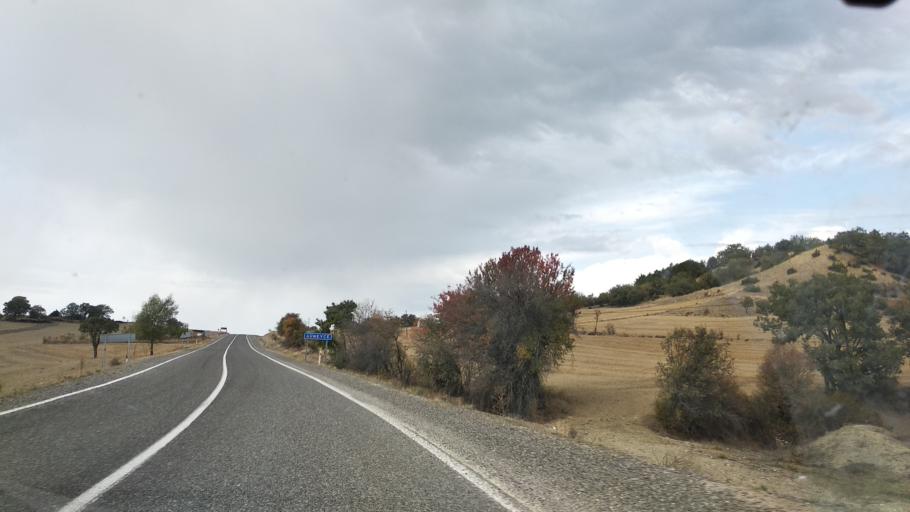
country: TR
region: Bolu
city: Seben
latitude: 40.3330
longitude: 31.4641
